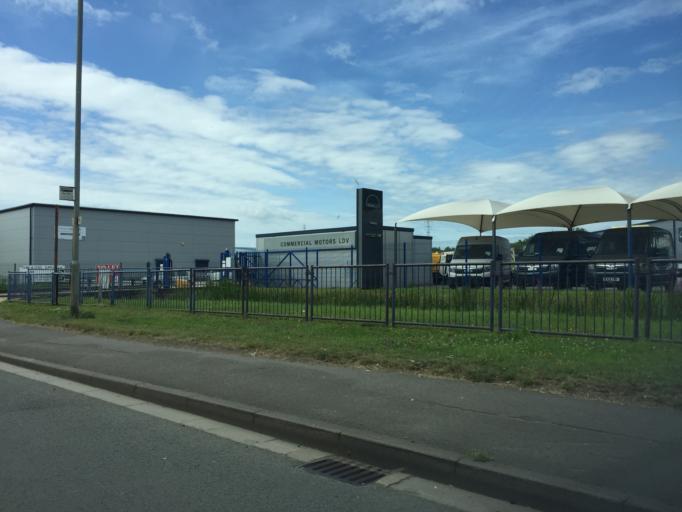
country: GB
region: Wales
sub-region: Newport
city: Newport
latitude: 51.5730
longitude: -2.9693
